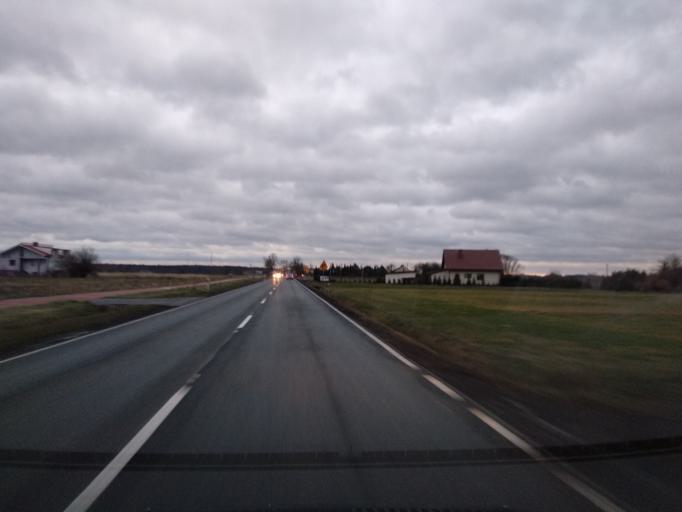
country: PL
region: Greater Poland Voivodeship
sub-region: Powiat koninski
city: Rychwal
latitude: 52.1068
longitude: 18.1674
